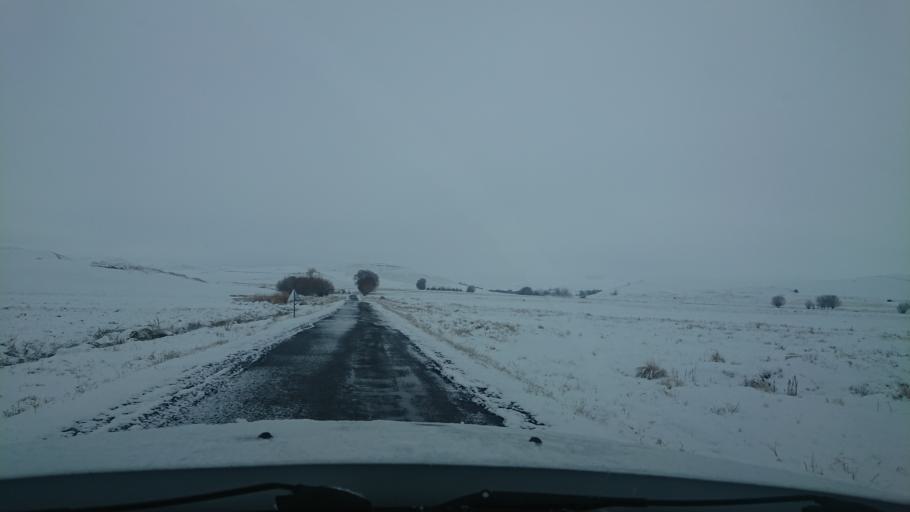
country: TR
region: Aksaray
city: Acipinar
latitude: 38.6832
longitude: 33.8643
